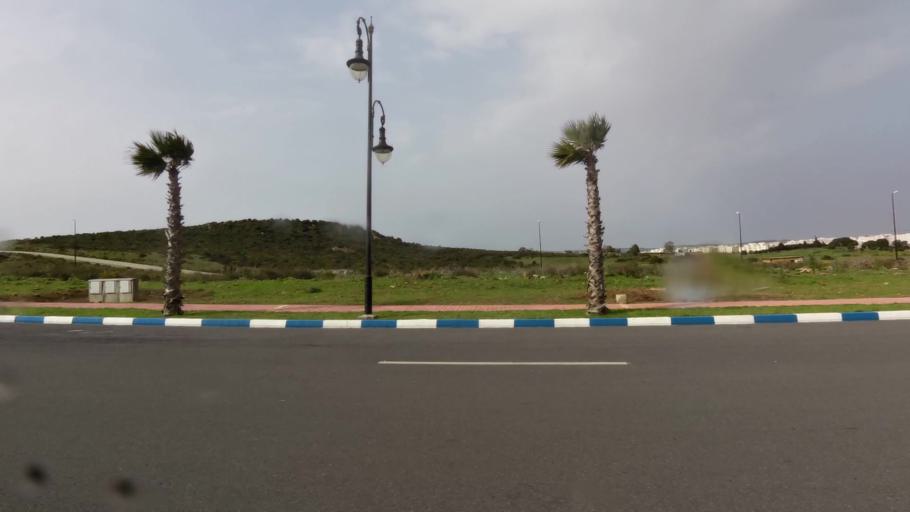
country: MA
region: Tanger-Tetouan
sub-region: Tanger-Assilah
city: Boukhalef
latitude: 35.6968
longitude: -5.9243
